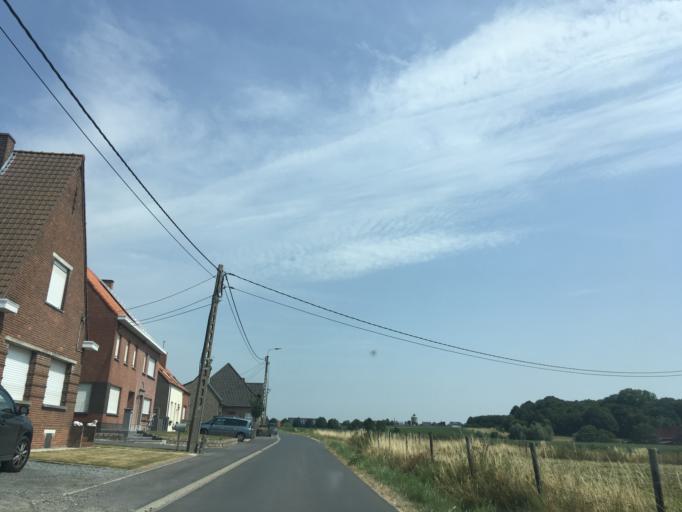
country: BE
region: Flanders
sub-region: Provincie West-Vlaanderen
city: Tielt
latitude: 50.9882
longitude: 3.3012
